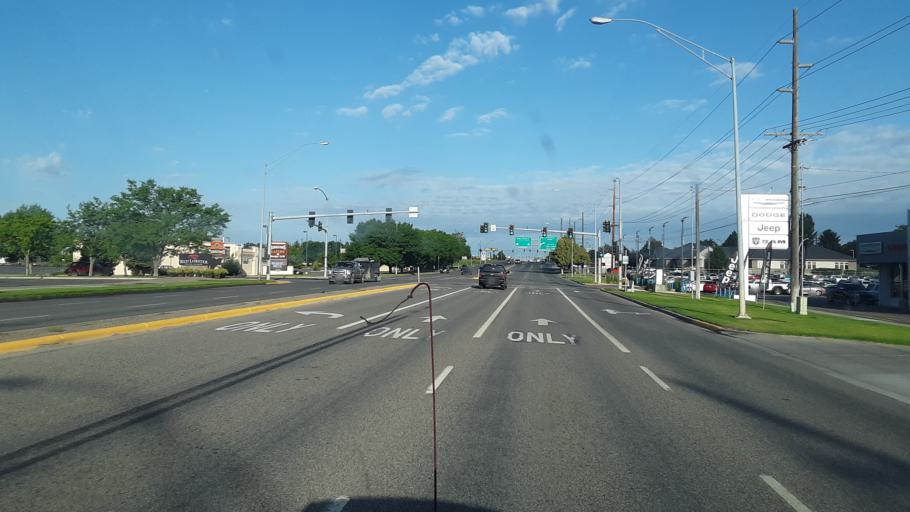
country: US
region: Montana
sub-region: Yellowstone County
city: Billings
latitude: 45.7552
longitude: -108.5717
